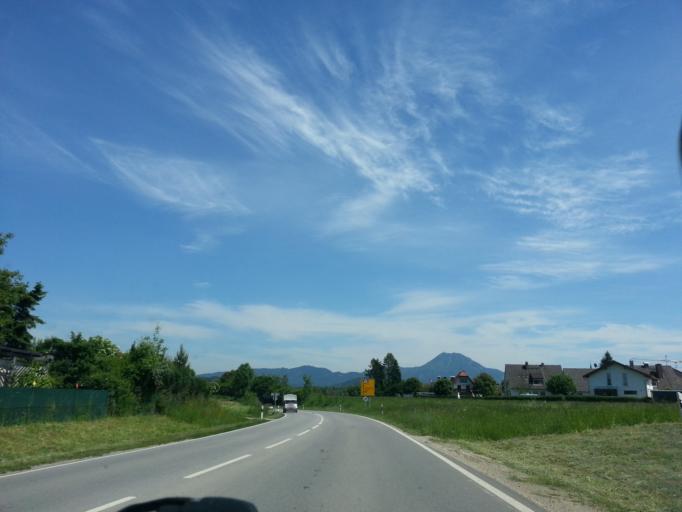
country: DE
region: Bavaria
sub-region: Upper Bavaria
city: Freilassing
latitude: 47.8534
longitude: 12.9806
